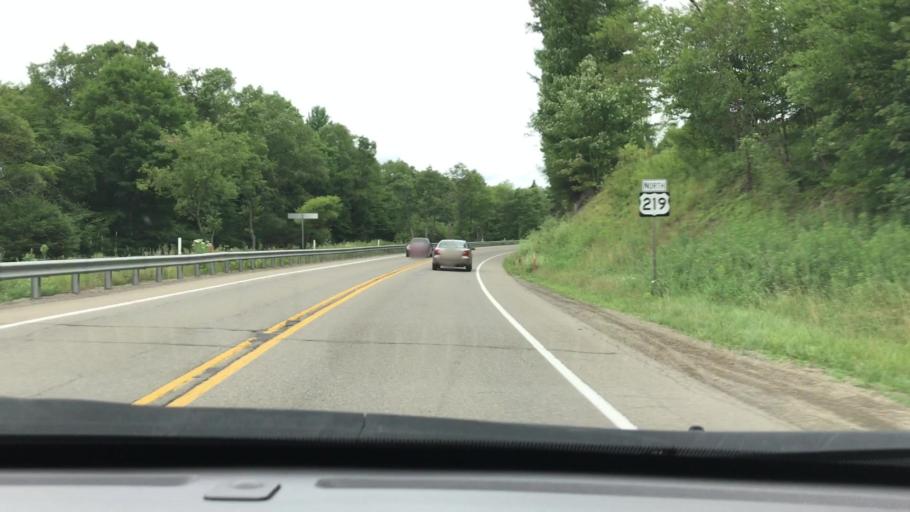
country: US
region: Pennsylvania
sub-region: Elk County
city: Johnsonburg
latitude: 41.5352
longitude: -78.6834
